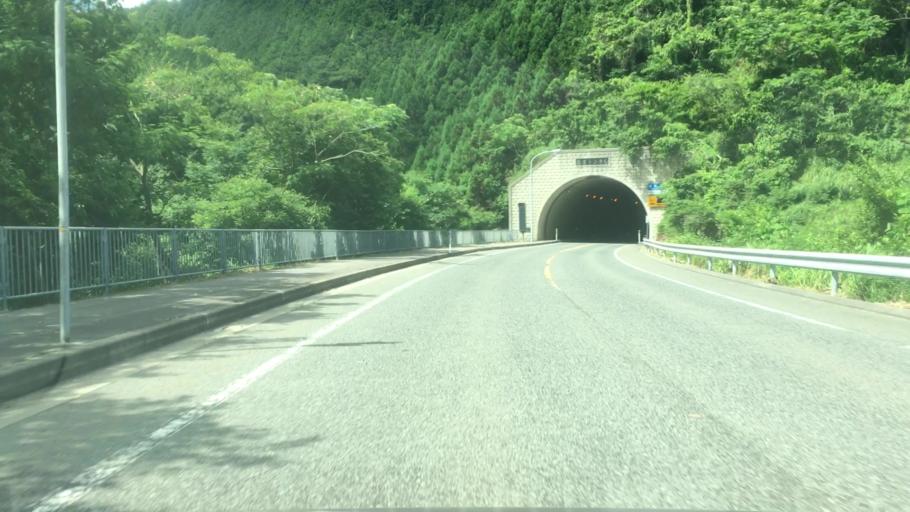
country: JP
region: Tottori
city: Tottori
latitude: 35.6175
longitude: 134.4157
